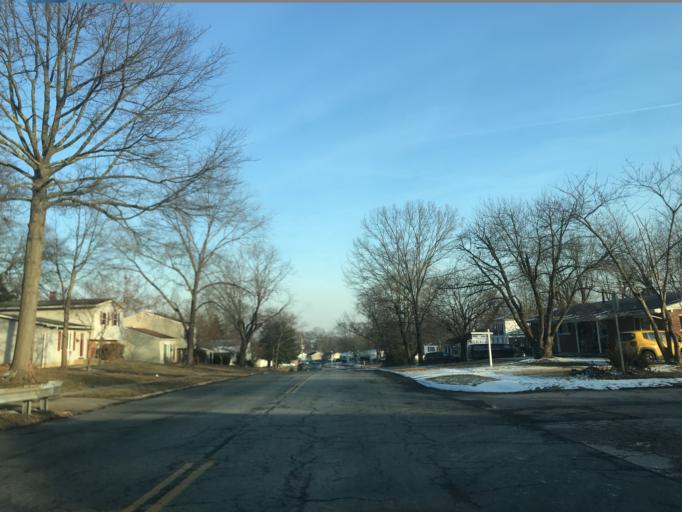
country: US
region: Maryland
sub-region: Harford County
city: Edgewood
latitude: 39.4255
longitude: -76.3062
